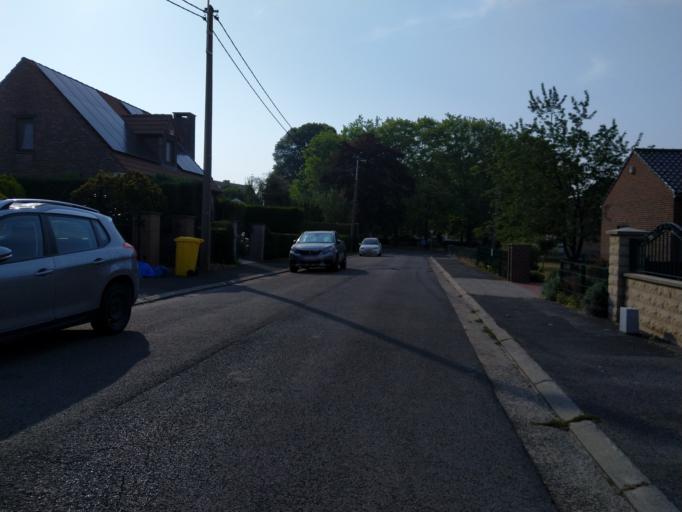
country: BE
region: Wallonia
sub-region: Province du Hainaut
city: Braine-le-Comte
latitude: 50.6085
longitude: 4.1460
